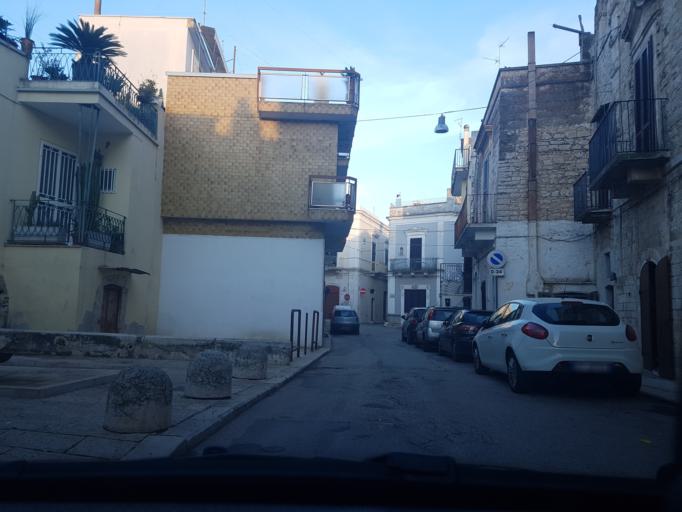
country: IT
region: Apulia
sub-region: Provincia di Bari
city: Bitritto
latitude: 41.0405
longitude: 16.8261
